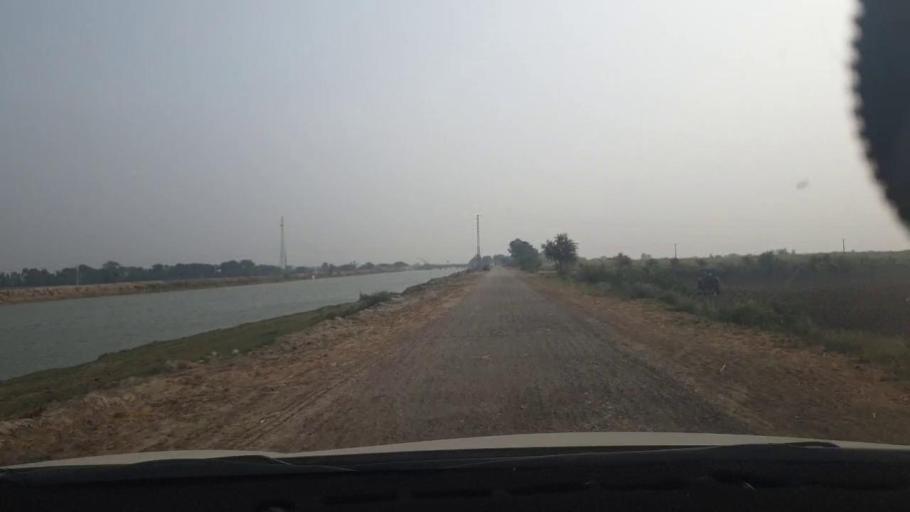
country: PK
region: Sindh
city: Tando Muhammad Khan
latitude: 24.9648
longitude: 68.4952
